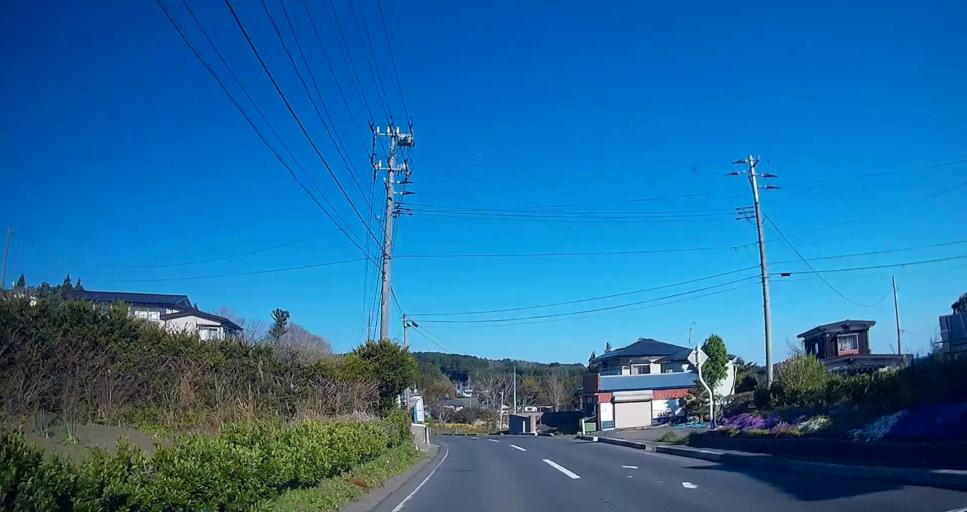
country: JP
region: Aomori
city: Hachinohe
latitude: 40.5160
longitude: 141.5891
